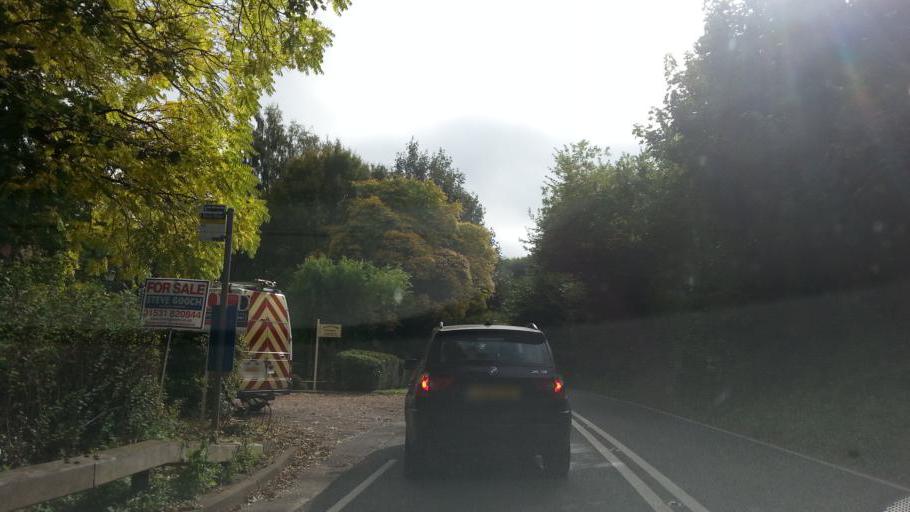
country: GB
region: England
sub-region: Gloucestershire
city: Mitcheldean
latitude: 51.8794
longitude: -2.4554
